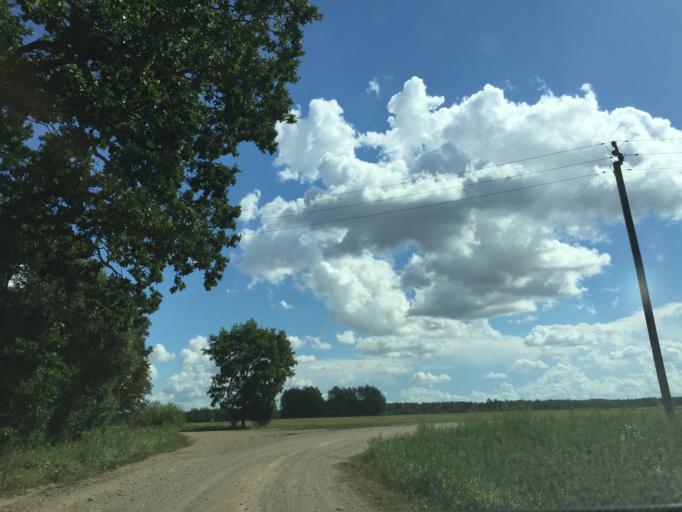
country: LV
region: Rundales
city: Pilsrundale
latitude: 56.3225
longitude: 23.9892
